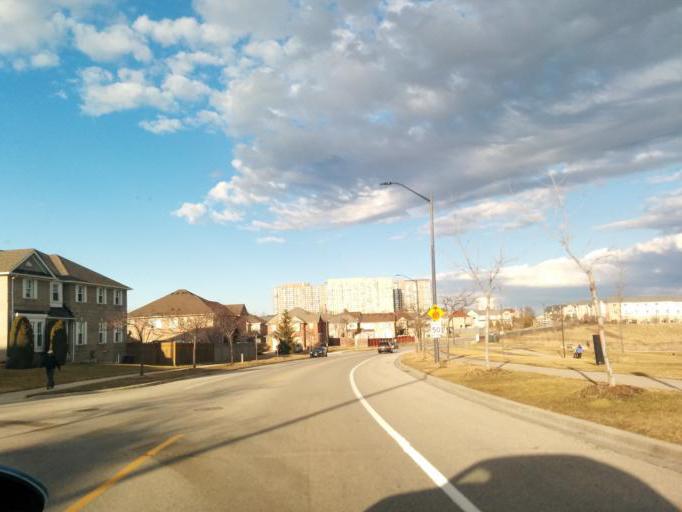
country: CA
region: Ontario
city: Mississauga
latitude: 43.5747
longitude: -79.6307
